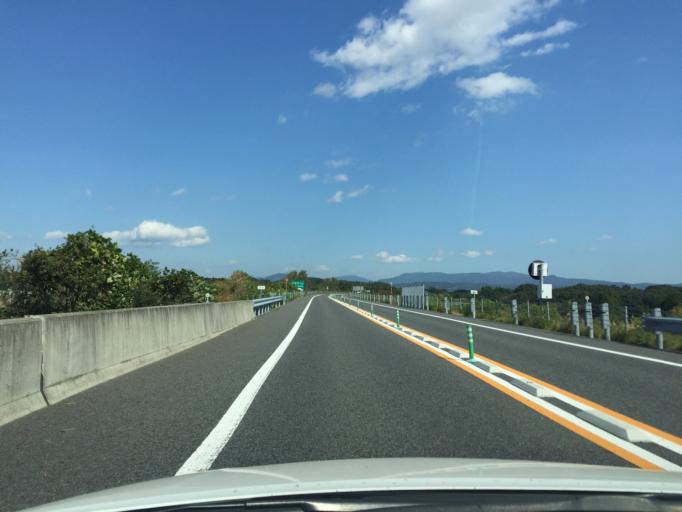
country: JP
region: Fukushima
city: Sukagawa
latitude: 37.1966
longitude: 140.3539
